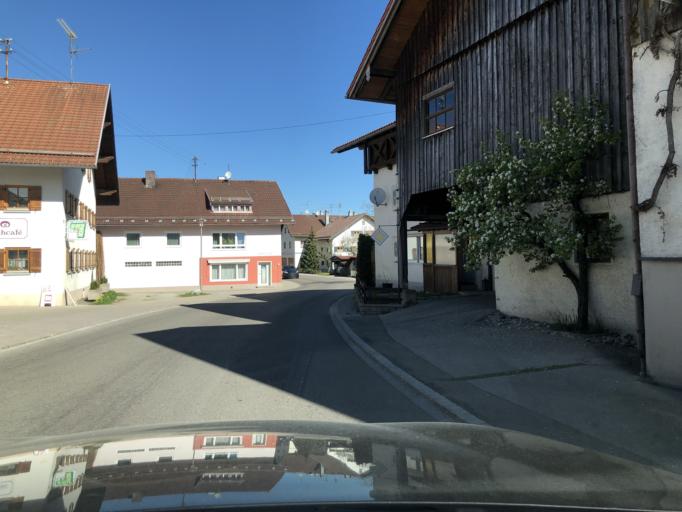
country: DE
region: Bavaria
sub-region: Swabia
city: Wald
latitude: 47.7469
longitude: 10.5745
